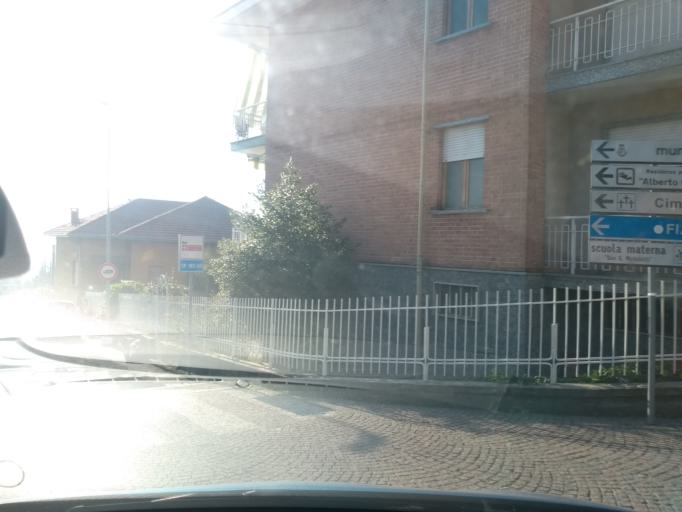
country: IT
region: Piedmont
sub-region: Provincia di Torino
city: Vallo Torinese
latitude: 45.2242
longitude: 7.4974
